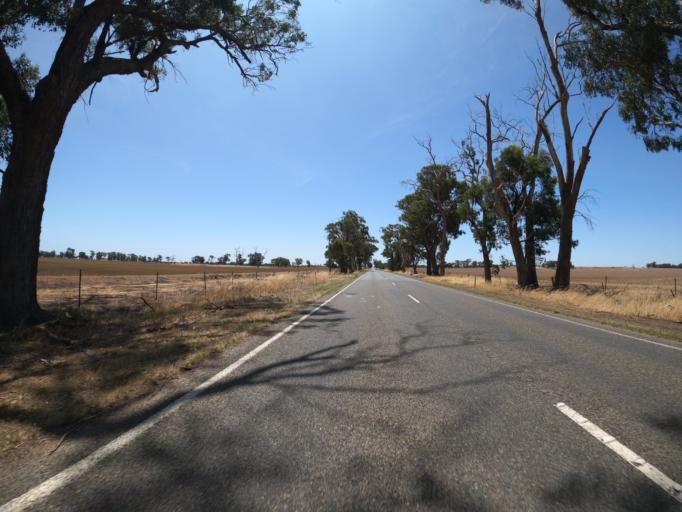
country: AU
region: Victoria
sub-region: Moira
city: Yarrawonga
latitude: -36.0607
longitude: 145.9955
